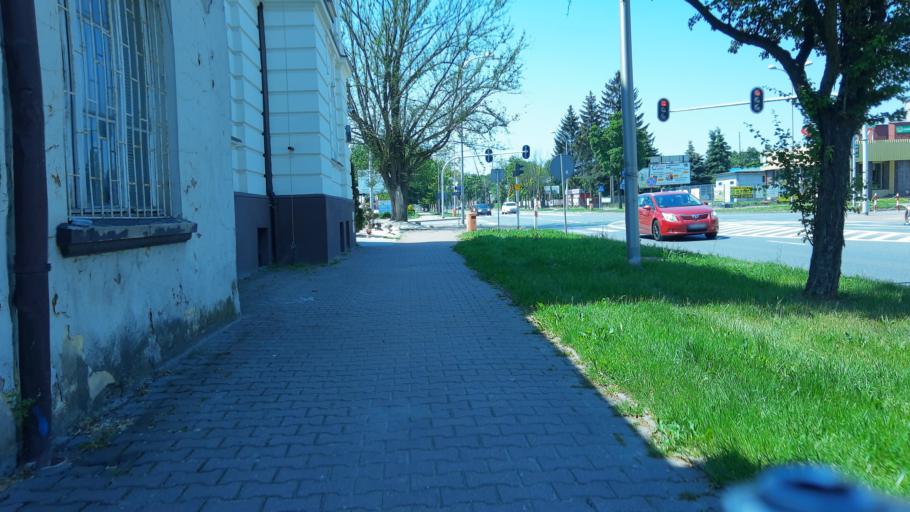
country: PL
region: Lodz Voivodeship
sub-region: Powiat sieradzki
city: Sieradz
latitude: 51.5953
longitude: 18.7267
